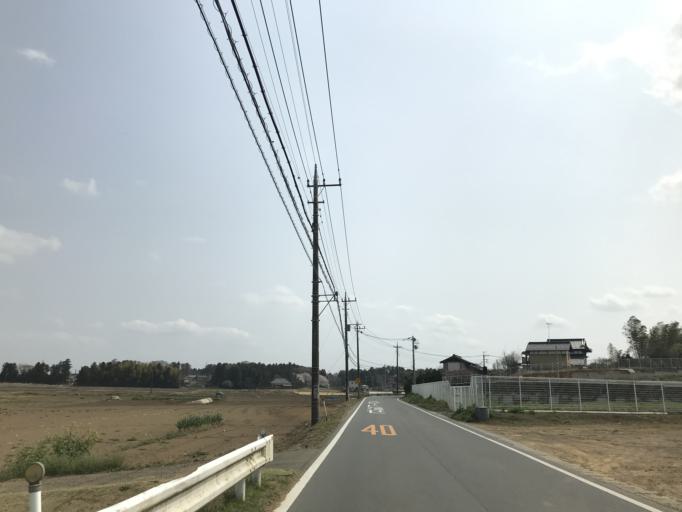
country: JP
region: Ibaraki
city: Ushiku
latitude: 36.0086
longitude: 140.0659
